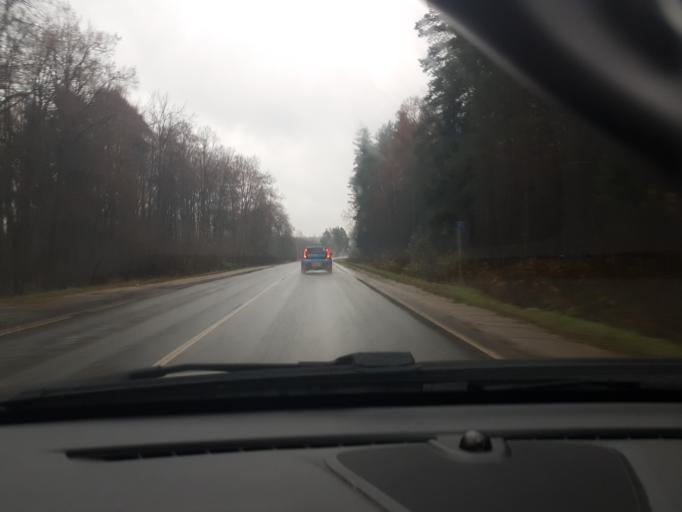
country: RU
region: Moskovskaya
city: Snegiri
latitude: 55.8511
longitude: 36.9474
